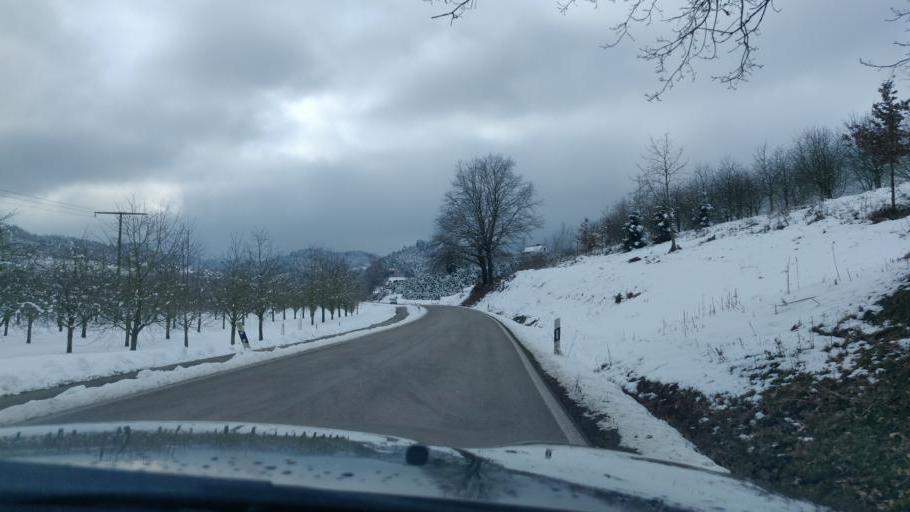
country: DE
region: Baden-Wuerttemberg
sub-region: Freiburg Region
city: Lautenbach
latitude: 48.5074
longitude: 8.0943
